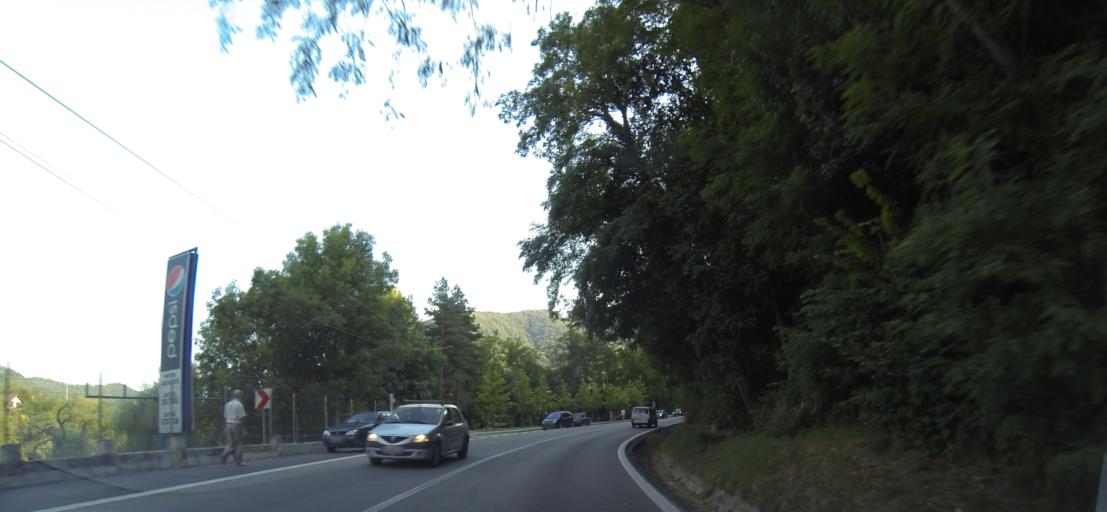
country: RO
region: Valcea
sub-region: Oras Calimanesti
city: Calimanesti
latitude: 45.2651
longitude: 24.3199
